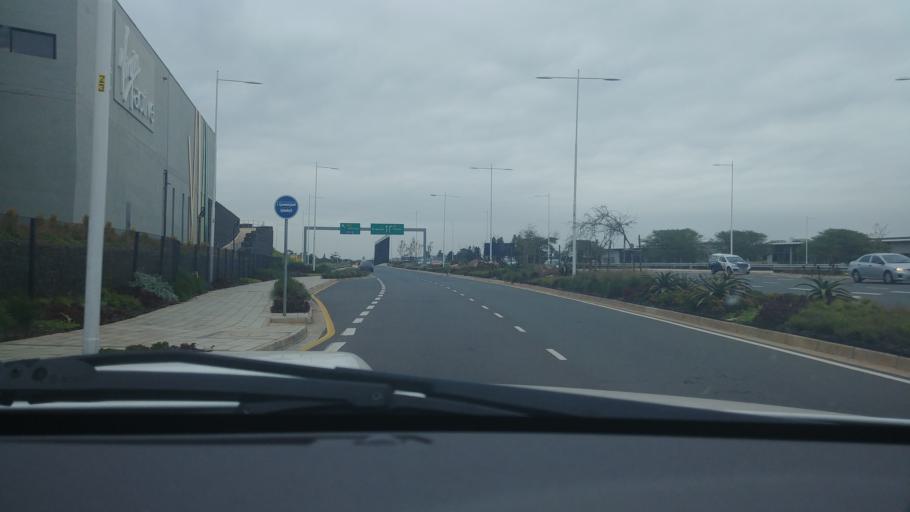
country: ZA
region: KwaZulu-Natal
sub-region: eThekwini Metropolitan Municipality
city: Durban
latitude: -29.7099
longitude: 31.0534
